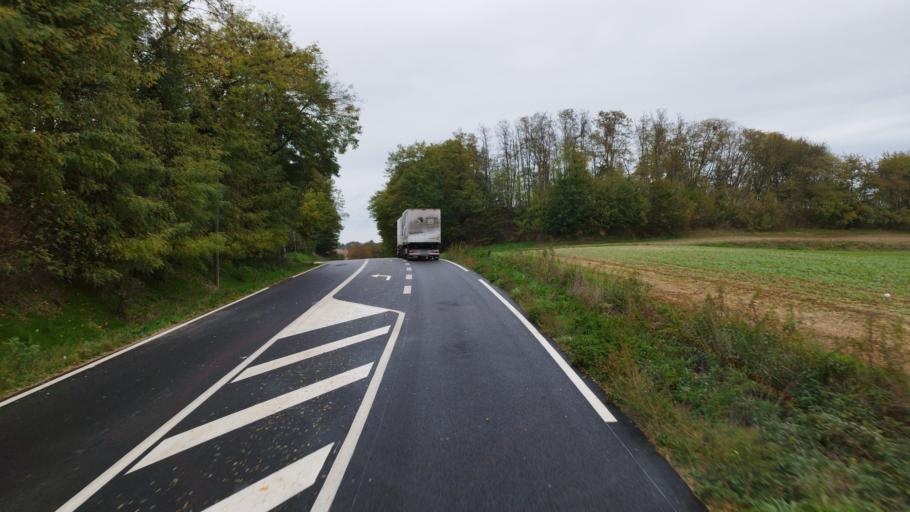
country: FR
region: Alsace
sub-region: Departement du Bas-Rhin
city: Seltz
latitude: 48.9238
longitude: 8.1027
